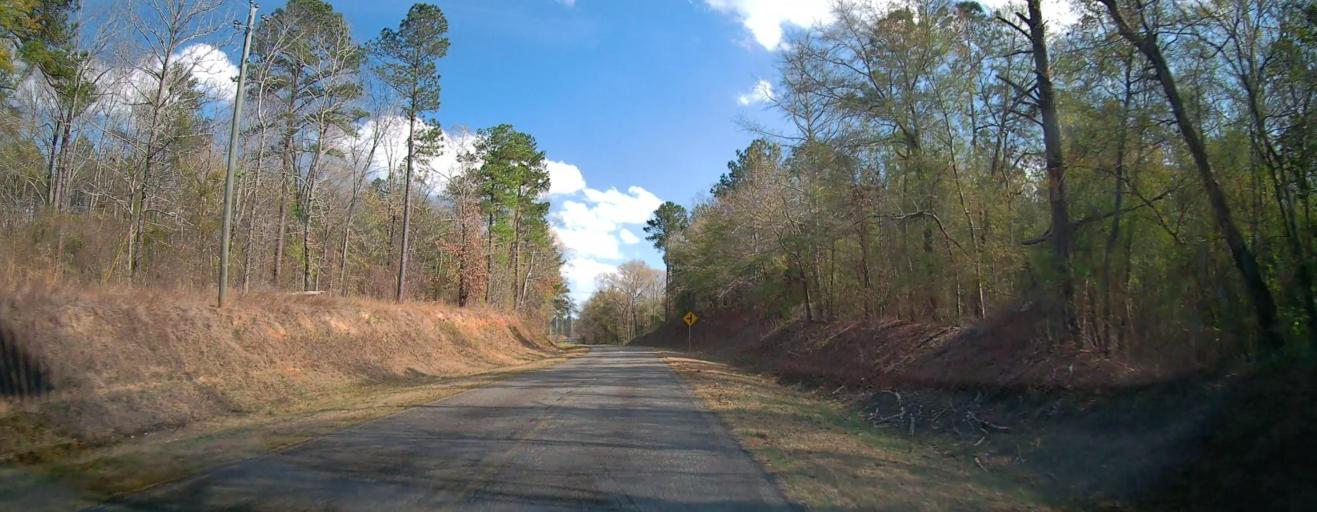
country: US
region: Georgia
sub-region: Twiggs County
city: Jeffersonville
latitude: 32.6654
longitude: -83.2318
